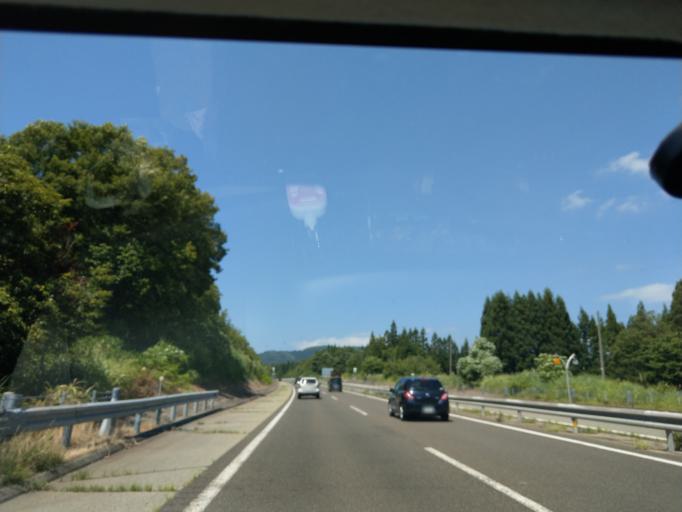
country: JP
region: Akita
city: Omagari
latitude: 39.4201
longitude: 140.4346
